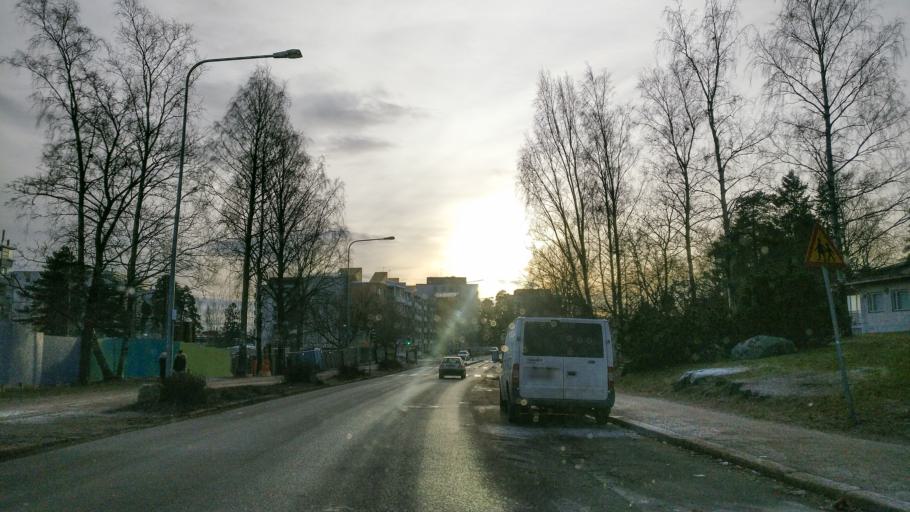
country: FI
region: Uusimaa
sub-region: Helsinki
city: Vantaa
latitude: 60.2017
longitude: 25.0598
